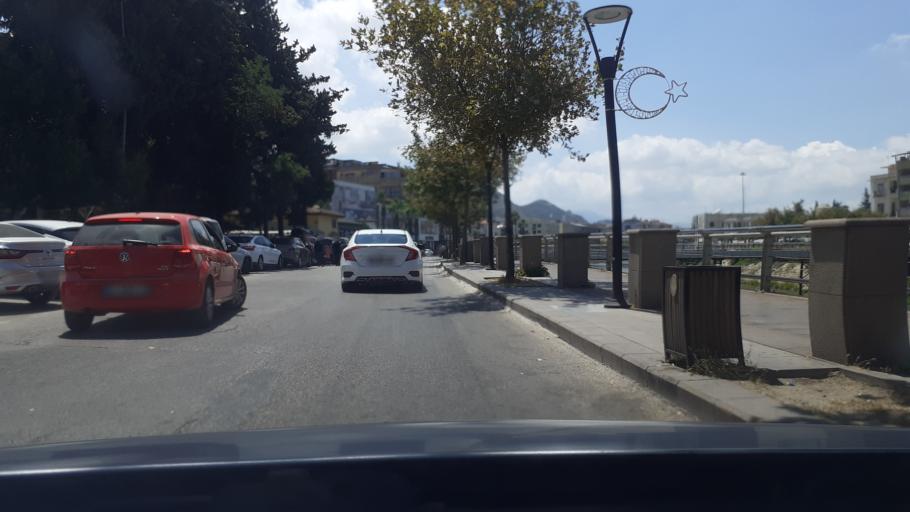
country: TR
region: Hatay
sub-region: Antakya Ilcesi
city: Antakya
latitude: 36.2052
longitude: 36.1621
